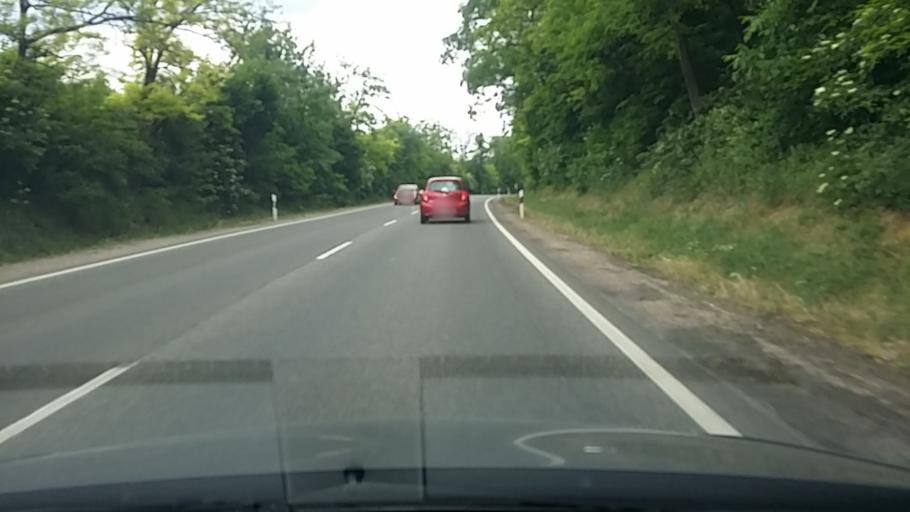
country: HU
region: Fejer
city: dunaujvaros
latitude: 46.9685
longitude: 18.9072
